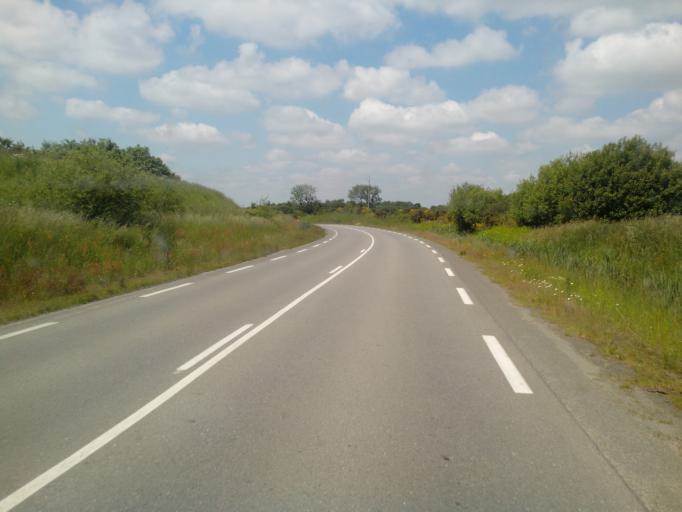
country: FR
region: Brittany
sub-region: Departement d'Ille-et-Vilaine
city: Saint-Etienne-en-Cogles
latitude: 48.3948
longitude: -1.3348
